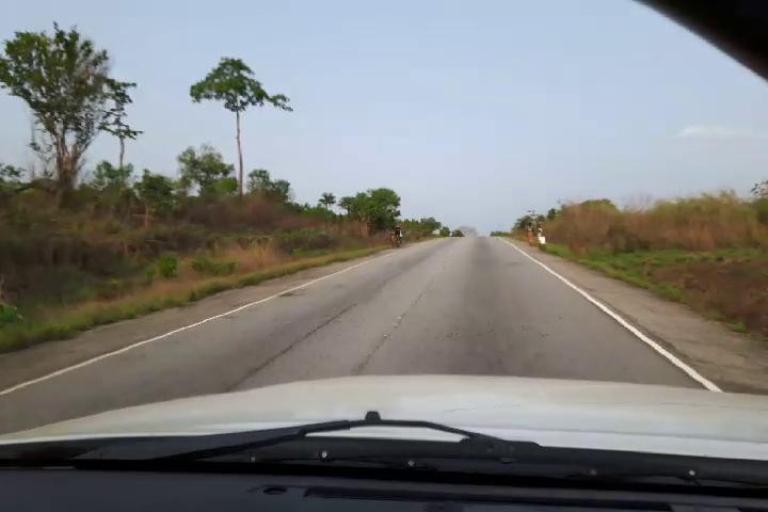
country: SL
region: Eastern Province
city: Blama
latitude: 7.9327
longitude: -11.5190
